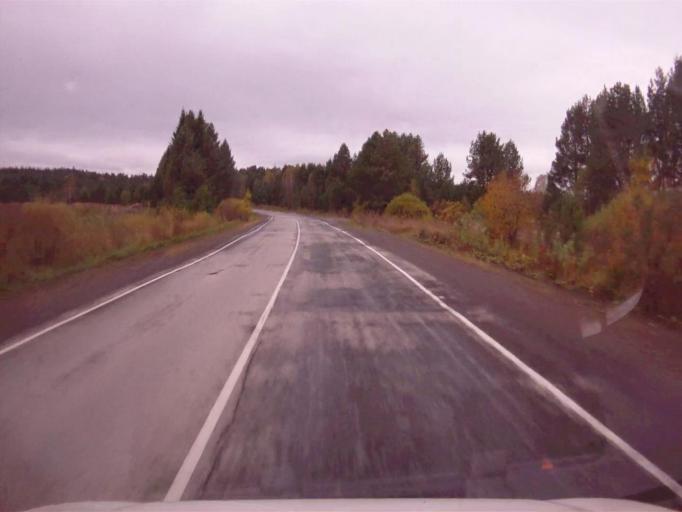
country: RU
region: Chelyabinsk
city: Nyazepetrovsk
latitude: 56.0672
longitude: 59.6963
